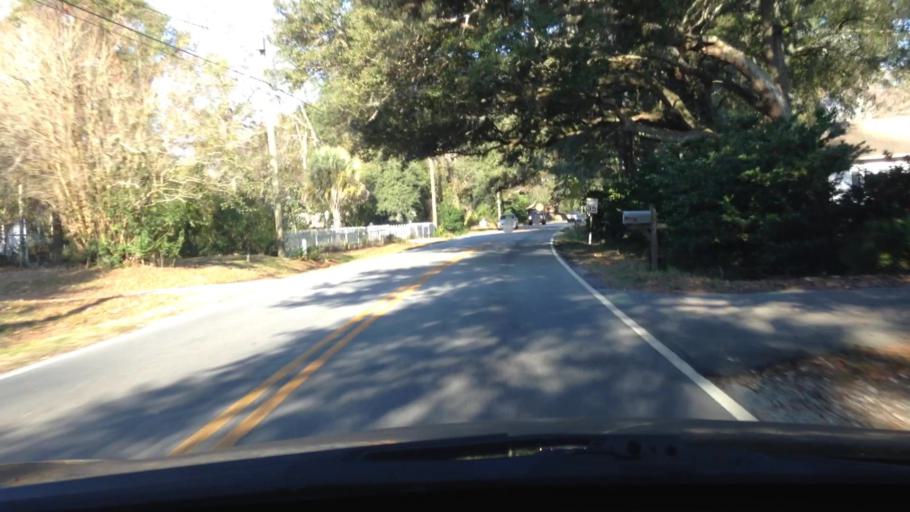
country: US
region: South Carolina
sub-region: Charleston County
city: Charleston
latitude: 32.7533
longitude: -79.9954
